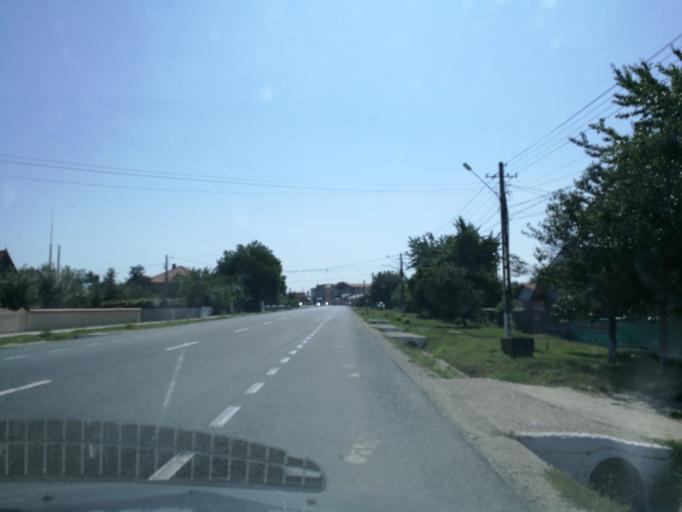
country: RO
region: Bacau
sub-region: Comuna Racaciuni
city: Racaciuni
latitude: 46.3368
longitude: 27.0019
